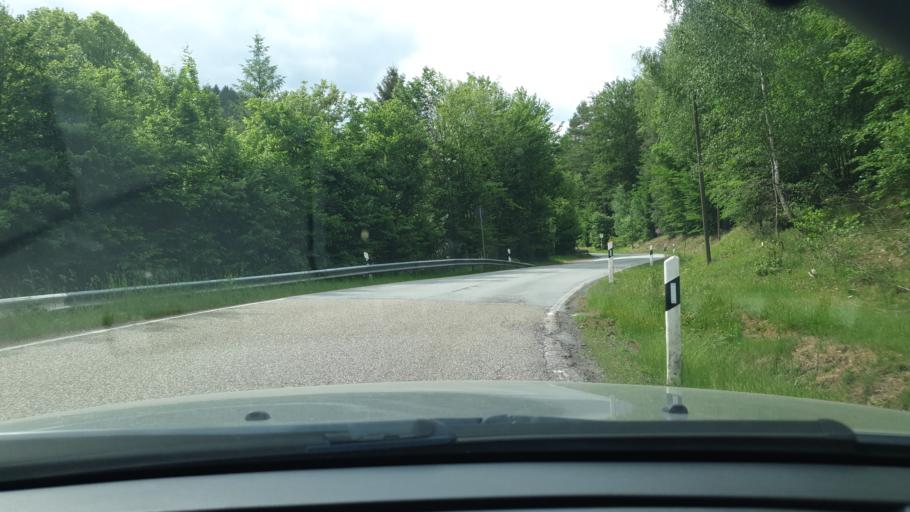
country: DE
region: Rheinland-Pfalz
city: Trippstadt
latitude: 49.3911
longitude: 7.7871
